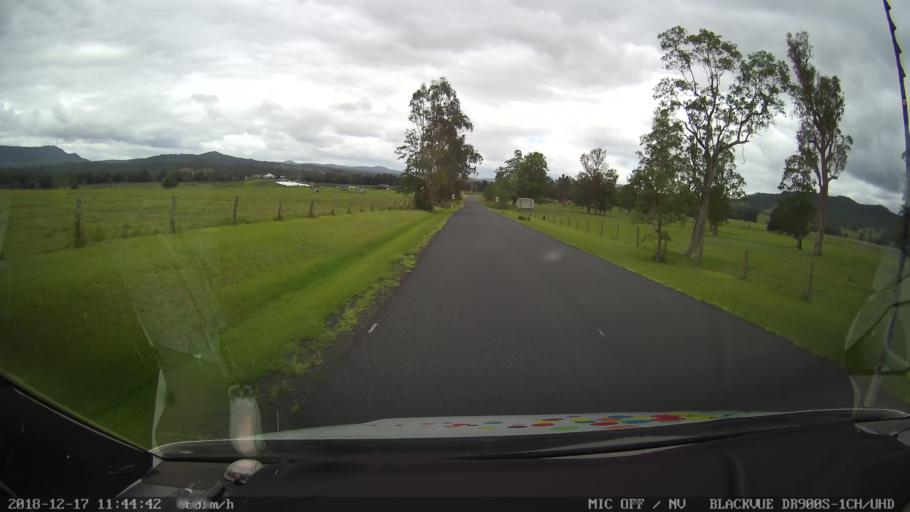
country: AU
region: New South Wales
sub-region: Kyogle
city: Kyogle
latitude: -28.6508
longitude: 152.5951
